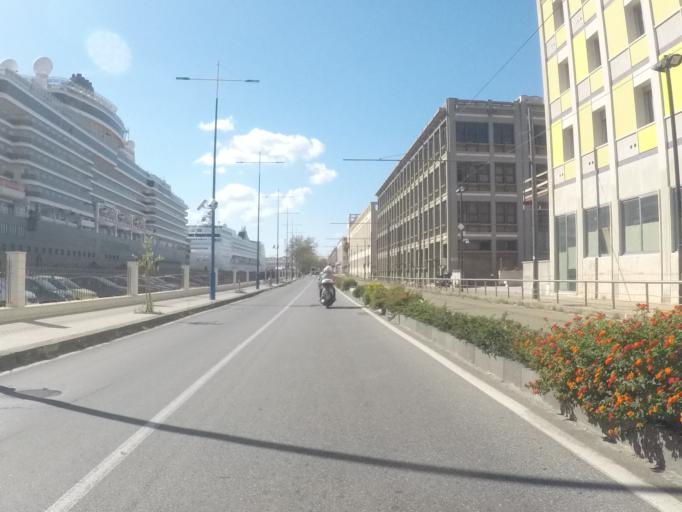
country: IT
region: Sicily
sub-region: Messina
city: Messina
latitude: 38.1960
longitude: 15.5576
